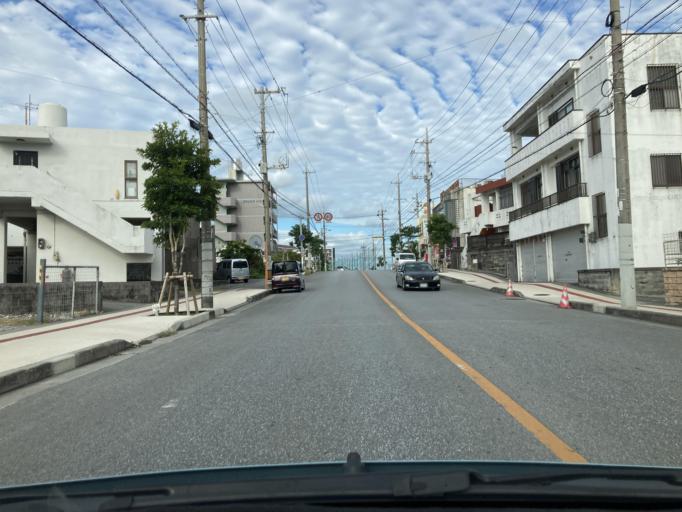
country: JP
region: Okinawa
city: Okinawa
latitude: 26.3370
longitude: 127.8201
